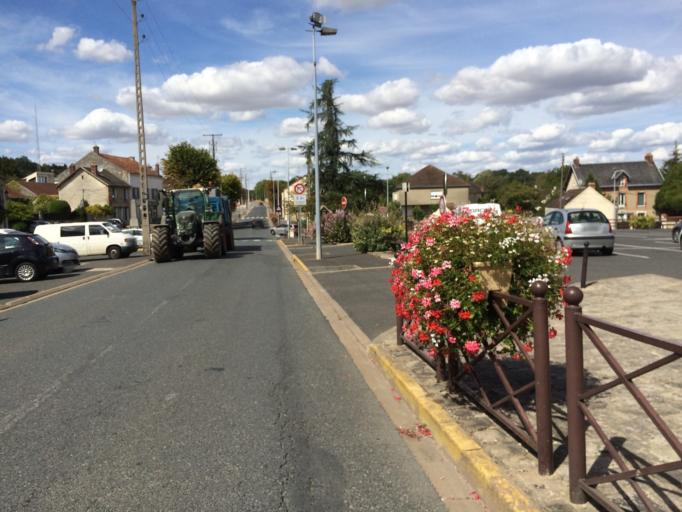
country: FR
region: Ile-de-France
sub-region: Departement de l'Essonne
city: Maisse
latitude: 48.3944
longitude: 2.3758
